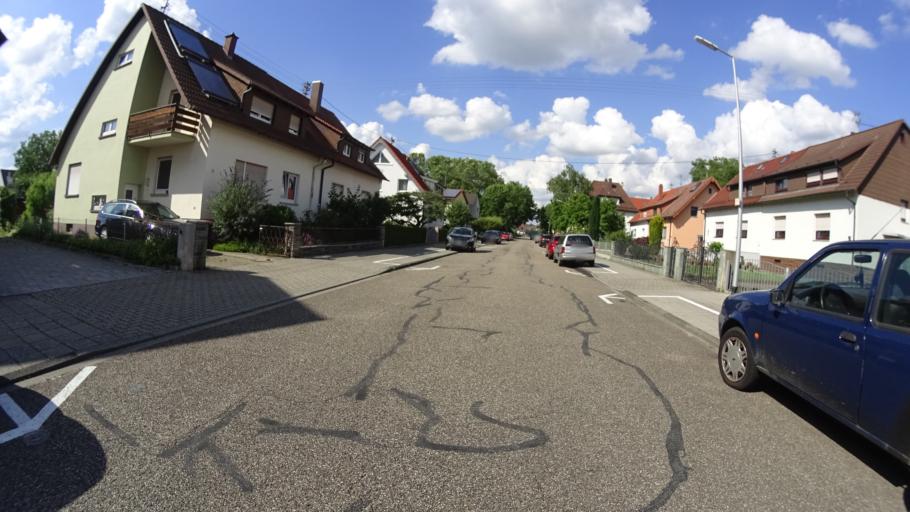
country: DE
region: Baden-Wuerttemberg
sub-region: Karlsruhe Region
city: Karlsruhe
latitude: 48.9882
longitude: 8.4593
